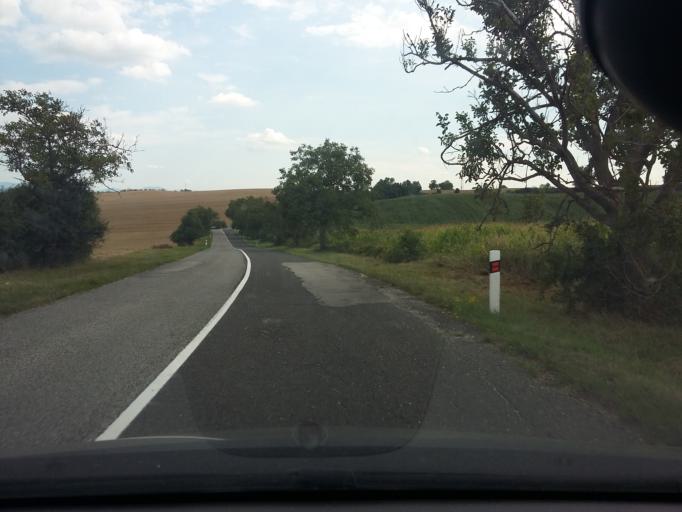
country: SK
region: Trnavsky
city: Gbely
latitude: 48.6685
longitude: 17.1478
